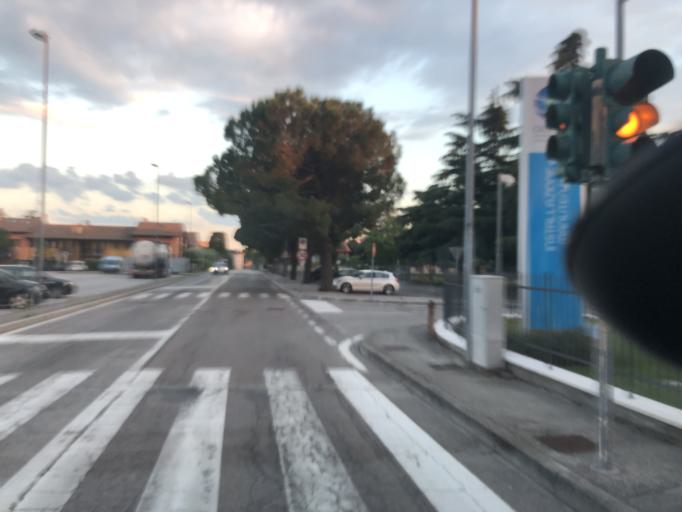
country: IT
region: Veneto
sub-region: Provincia di Verona
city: Settimo
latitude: 45.4803
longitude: 10.9032
